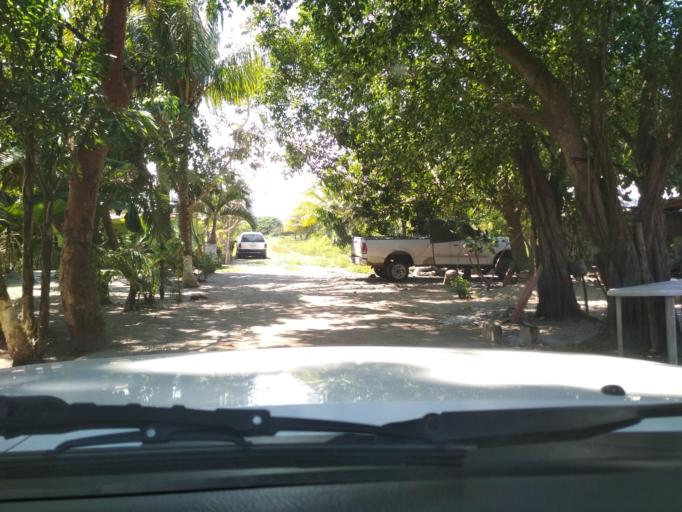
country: MX
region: Veracruz
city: Anton Lizardo
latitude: 19.0204
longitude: -95.9678
